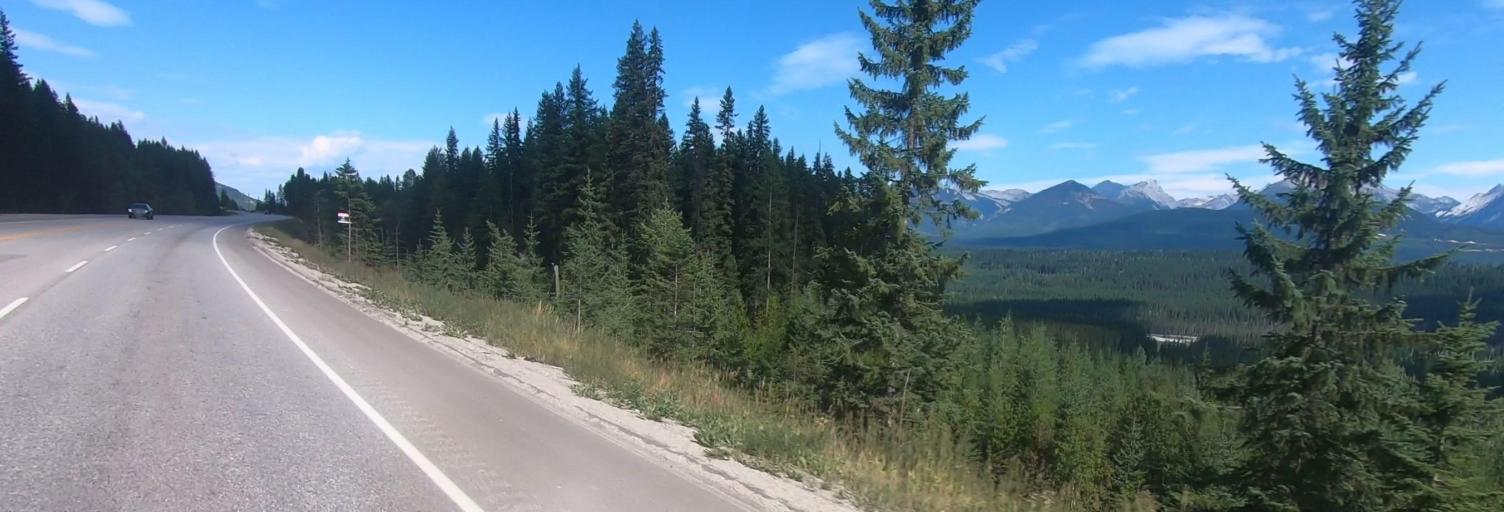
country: CA
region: British Columbia
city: Golden
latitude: 51.4892
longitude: -117.1998
